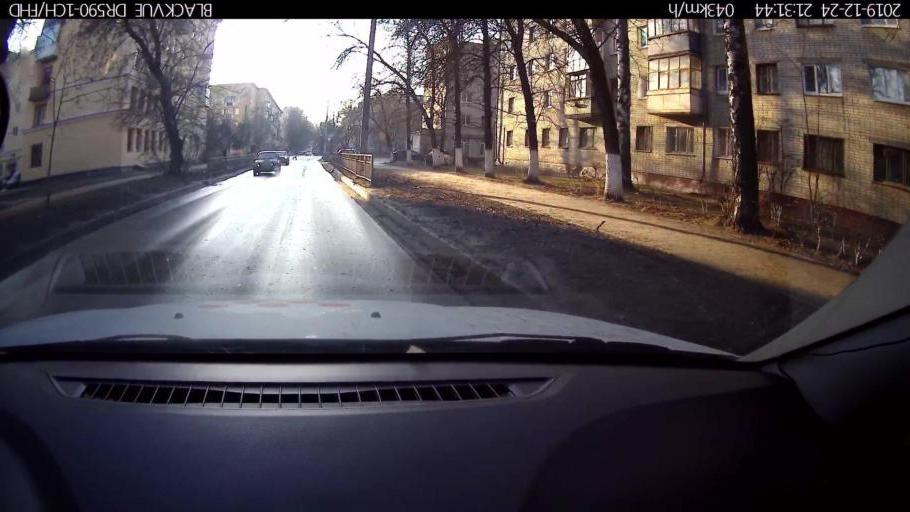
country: RU
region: Nizjnij Novgorod
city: Gorbatovka
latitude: 56.2474
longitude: 43.8472
